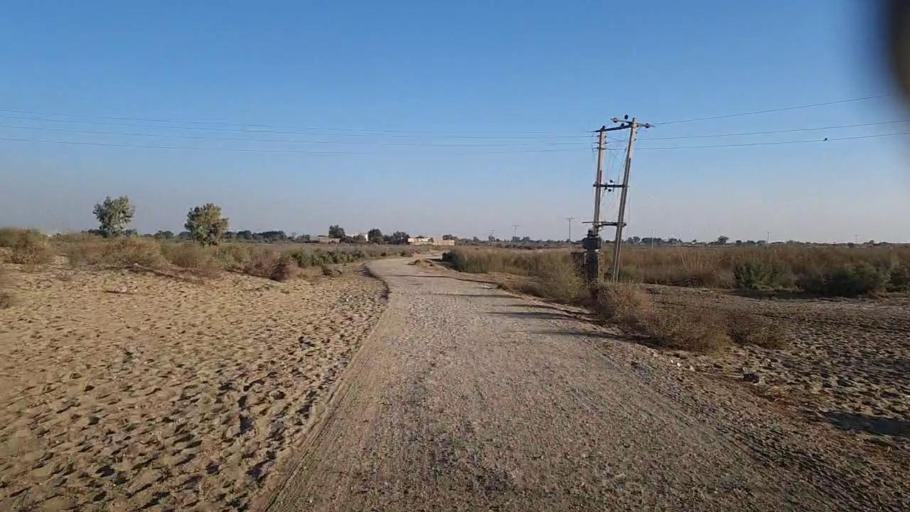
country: PK
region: Sindh
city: Khairpur
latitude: 27.8905
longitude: 69.7065
